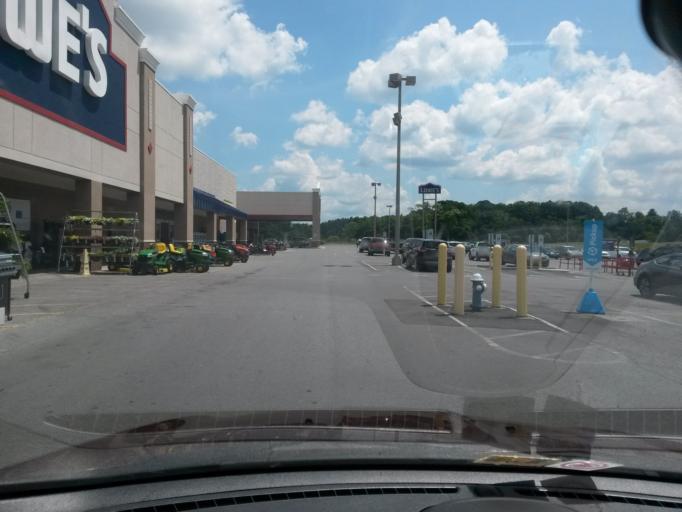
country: US
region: West Virginia
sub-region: Mercer County
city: Princeton
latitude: 37.3649
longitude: -81.0504
